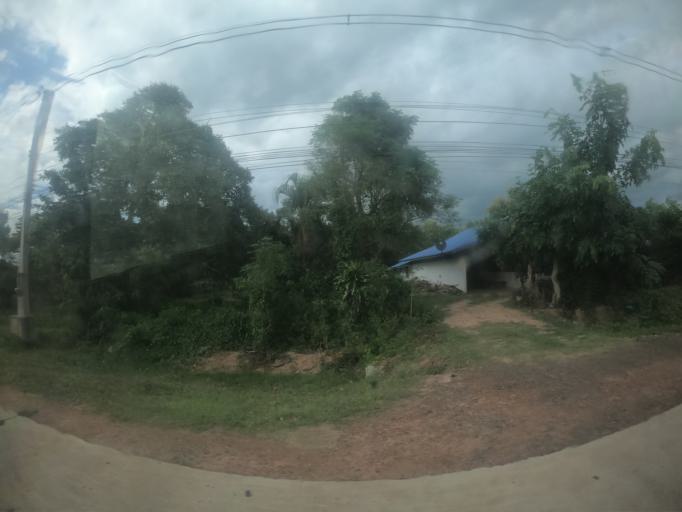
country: TH
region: Surin
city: Kap Choeng
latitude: 14.5481
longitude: 103.5123
